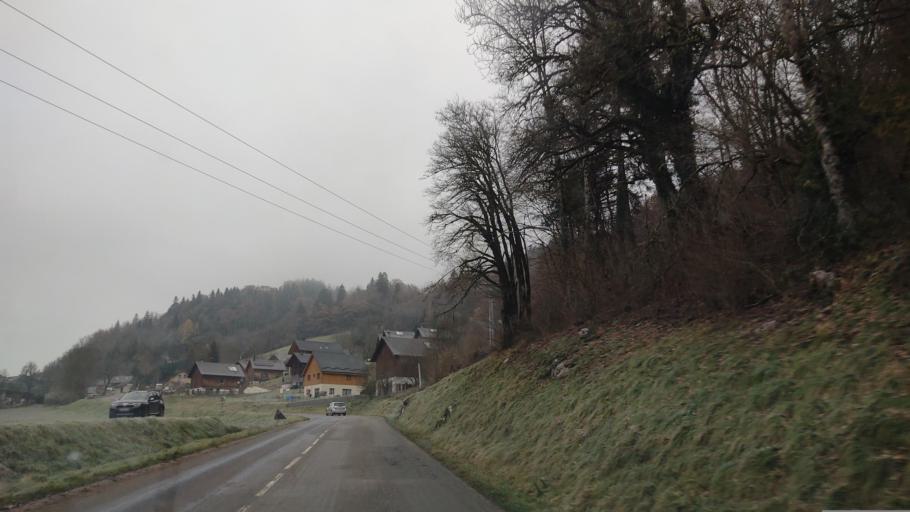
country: FR
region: Rhone-Alpes
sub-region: Departement de la Haute-Savoie
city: Doussard
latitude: 45.6763
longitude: 6.1448
